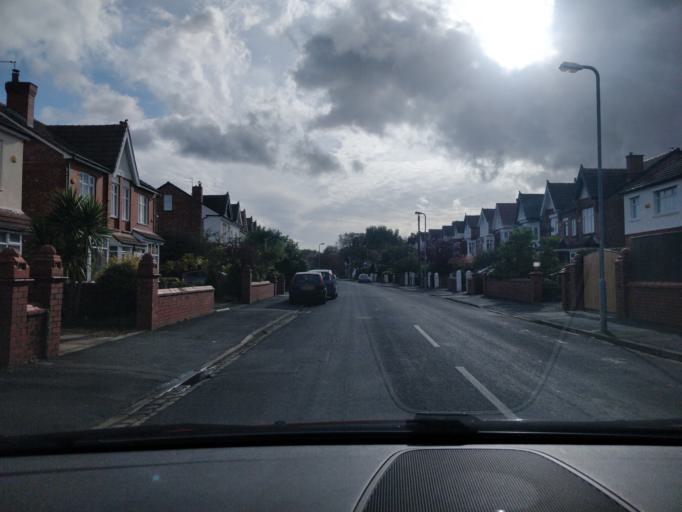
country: GB
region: England
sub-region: Sefton
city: Southport
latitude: 53.6236
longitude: -3.0167
